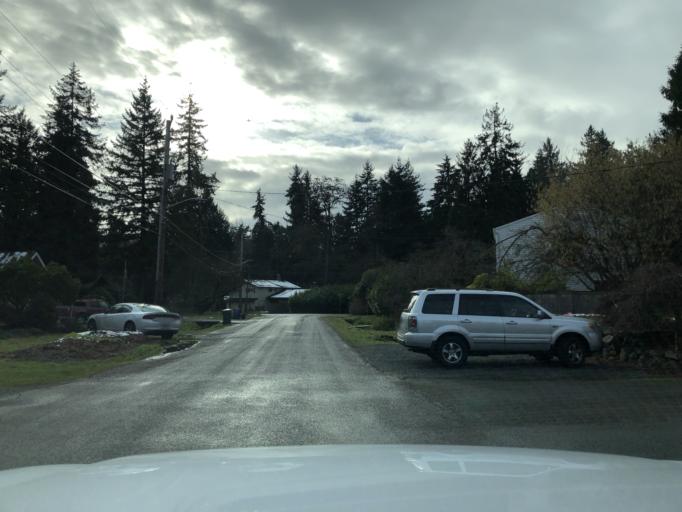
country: US
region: Washington
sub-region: King County
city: Shoreline
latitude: 47.7255
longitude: -122.3109
